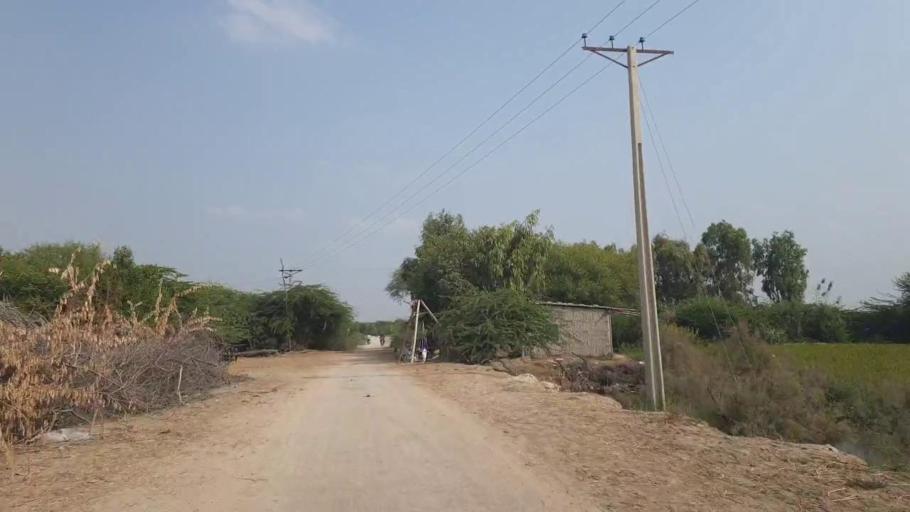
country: PK
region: Sindh
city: Badin
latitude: 24.5493
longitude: 68.7267
